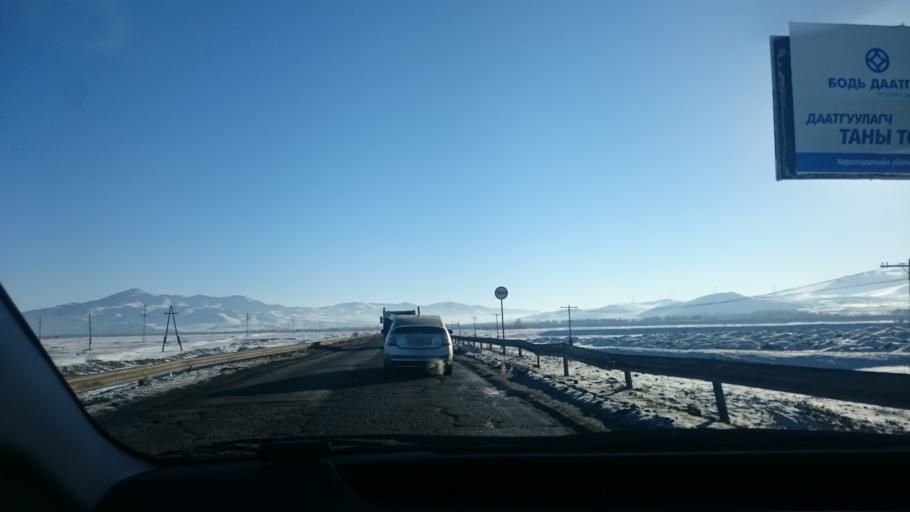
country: MN
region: Ulaanbaatar
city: Ulaanbaatar
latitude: 47.9003
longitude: 107.0355
